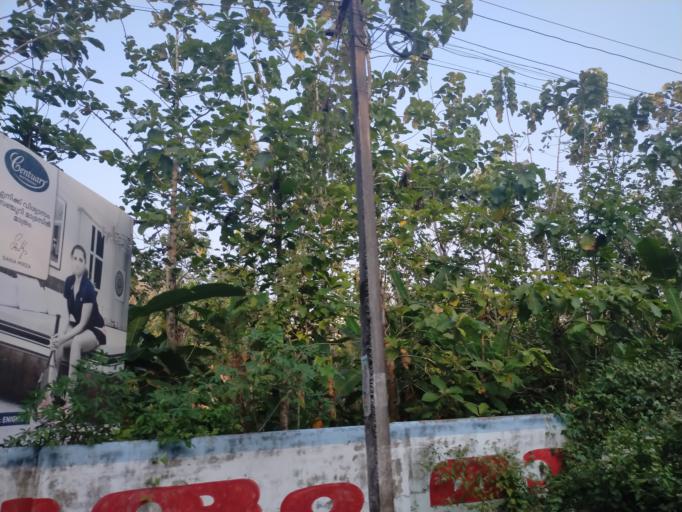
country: IN
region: Kerala
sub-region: Kottayam
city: Vaikam
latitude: 9.7504
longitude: 76.5064
